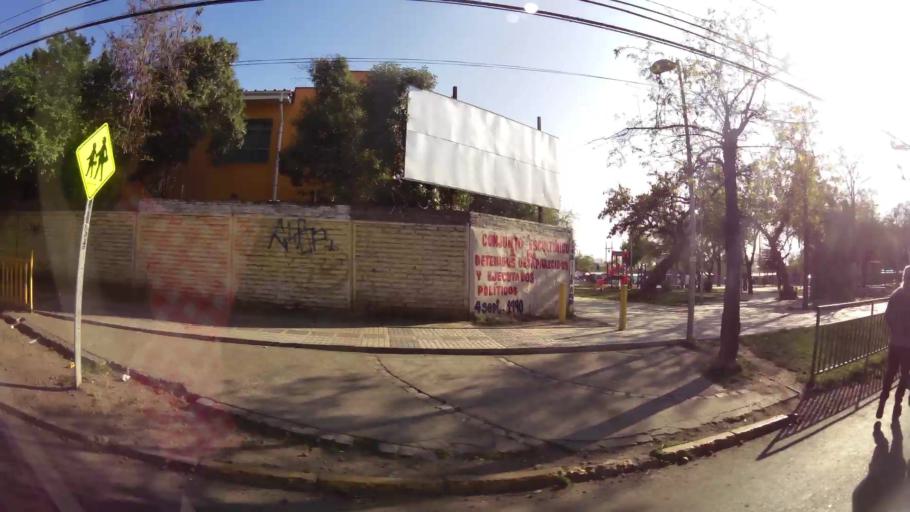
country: CL
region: Santiago Metropolitan
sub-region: Provincia de Santiago
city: Santiago
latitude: -33.4902
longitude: -70.6320
